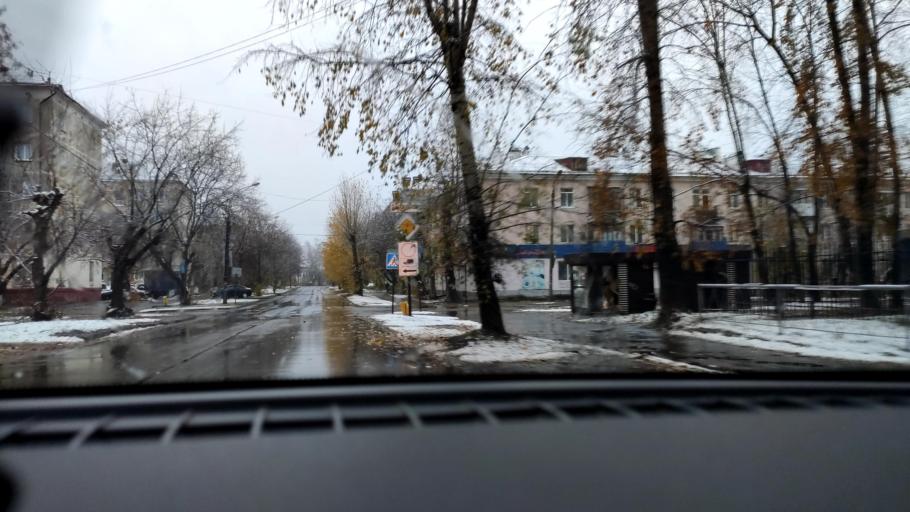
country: RU
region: Perm
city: Kultayevo
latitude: 58.0033
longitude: 55.9502
